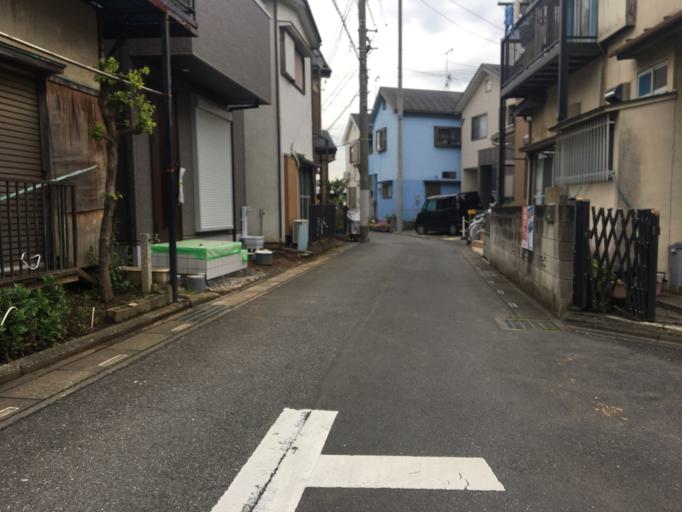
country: JP
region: Saitama
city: Oi
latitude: 35.8497
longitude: 139.5473
